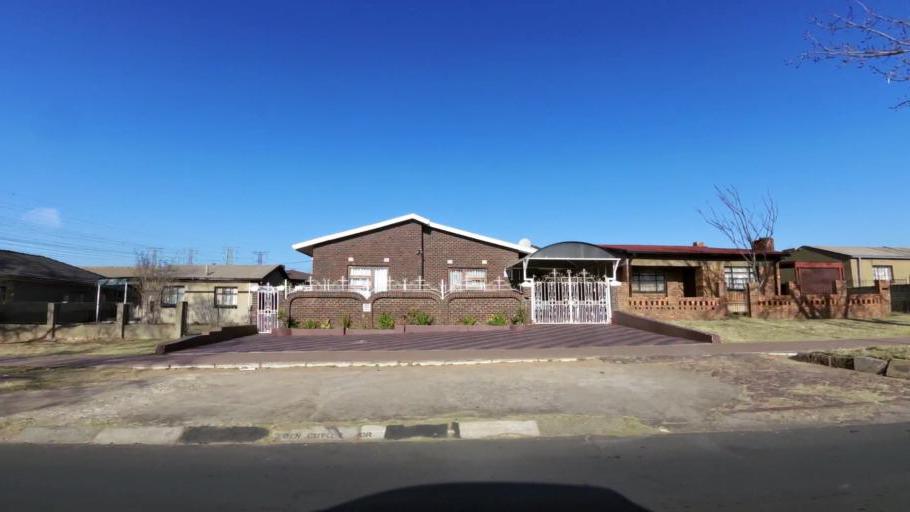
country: ZA
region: Gauteng
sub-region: City of Johannesburg Metropolitan Municipality
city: Soweto
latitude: -26.2354
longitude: 27.9405
